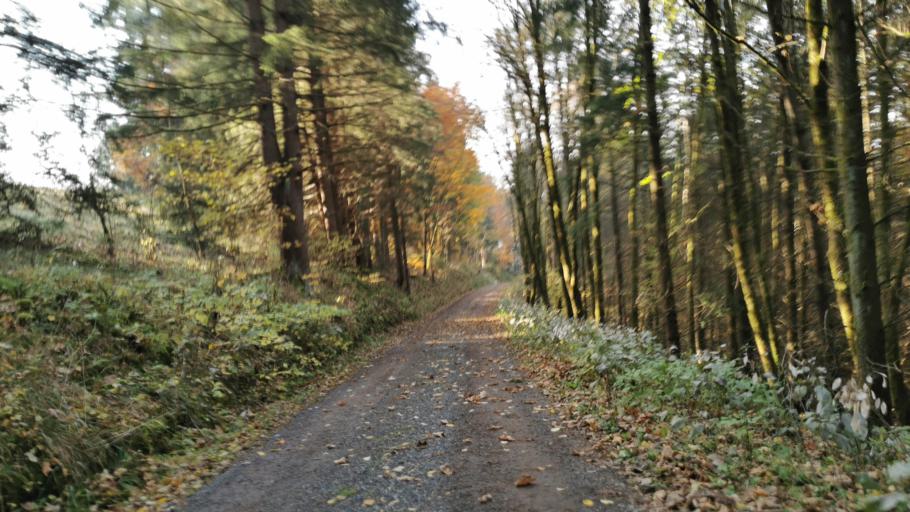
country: DE
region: Bavaria
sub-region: Upper Franconia
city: Nordhalben
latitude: 50.3635
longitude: 11.4980
